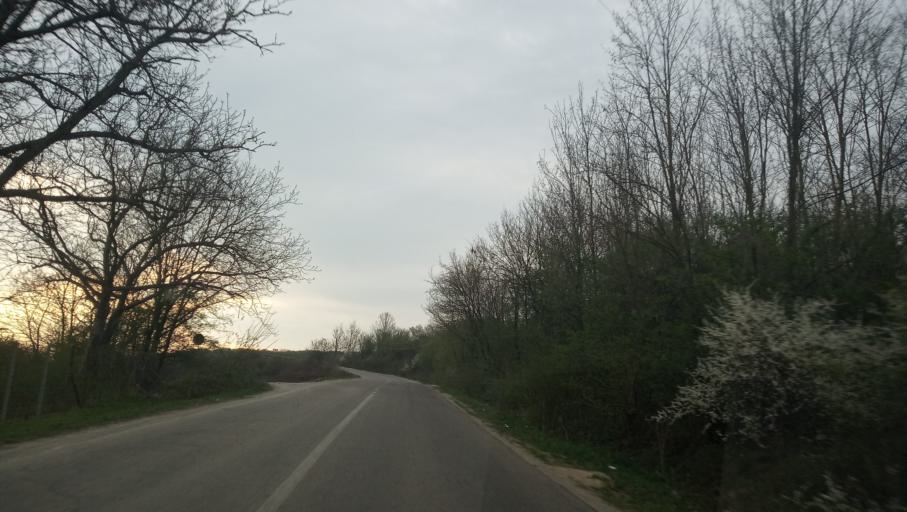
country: RO
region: Bihor
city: Hidiselu de Sus
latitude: 46.9262
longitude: 22.0516
